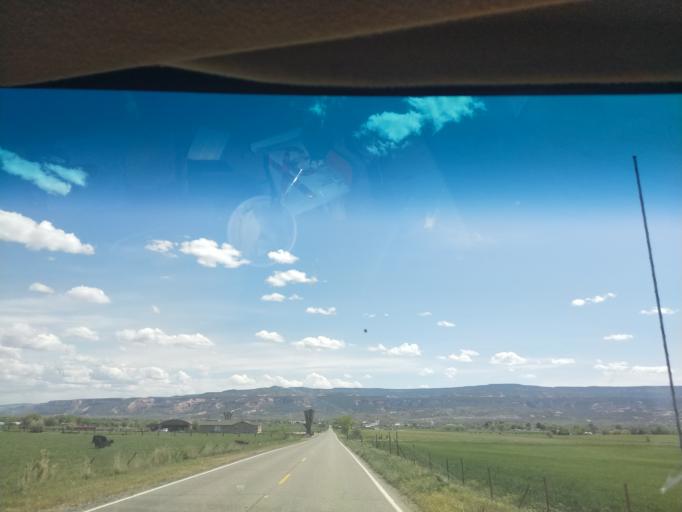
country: US
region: Colorado
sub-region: Mesa County
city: Fruita
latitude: 39.1875
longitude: -108.7570
